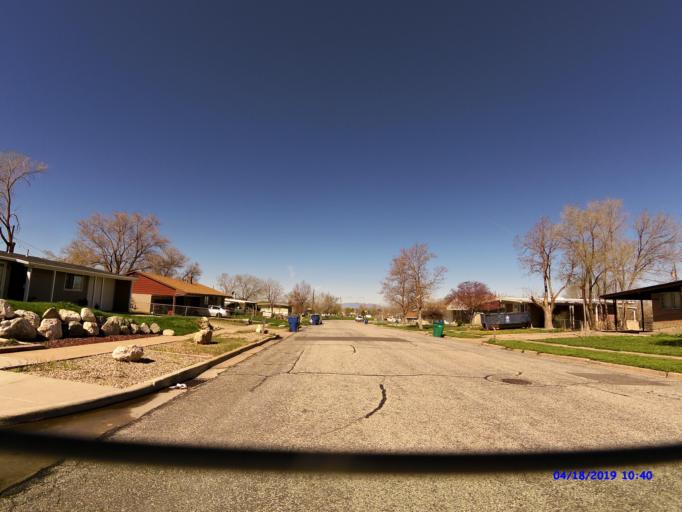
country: US
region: Utah
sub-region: Weber County
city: Harrisville
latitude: 41.2705
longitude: -111.9604
